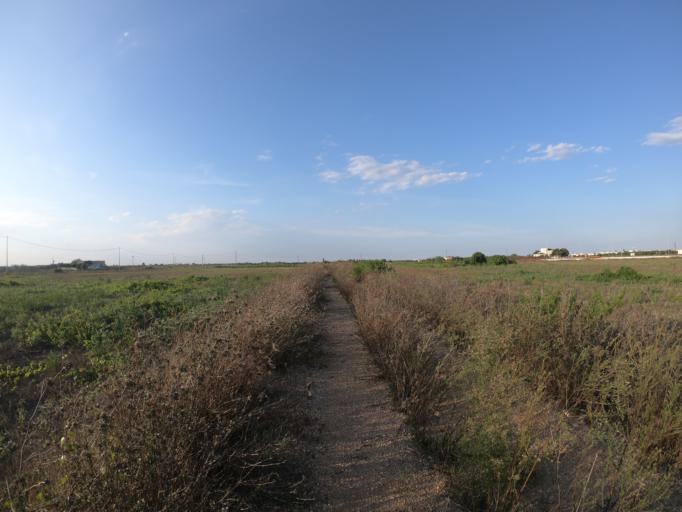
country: IT
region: Apulia
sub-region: Provincia di Lecce
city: Nardo
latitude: 40.1794
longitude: 18.0130
